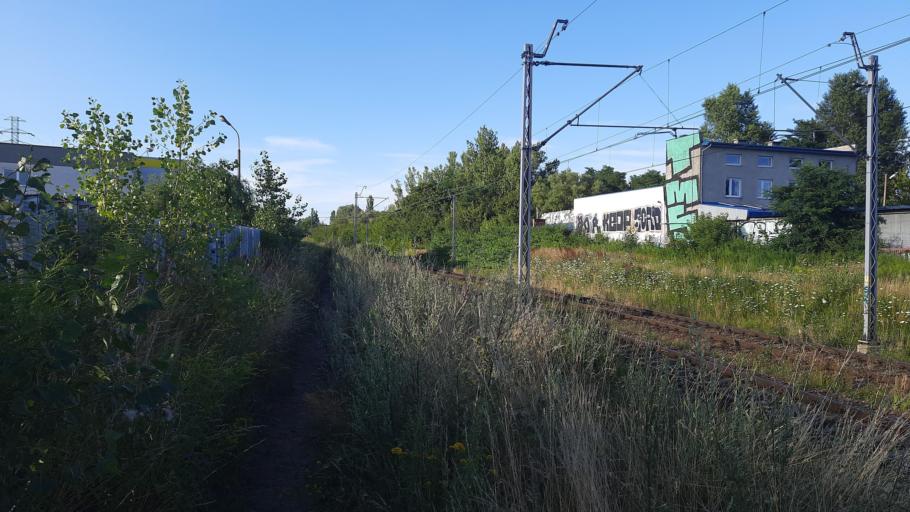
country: PL
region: Lodz Voivodeship
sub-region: Powiat lodzki wschodni
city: Starowa Gora
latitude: 51.7289
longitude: 19.5086
